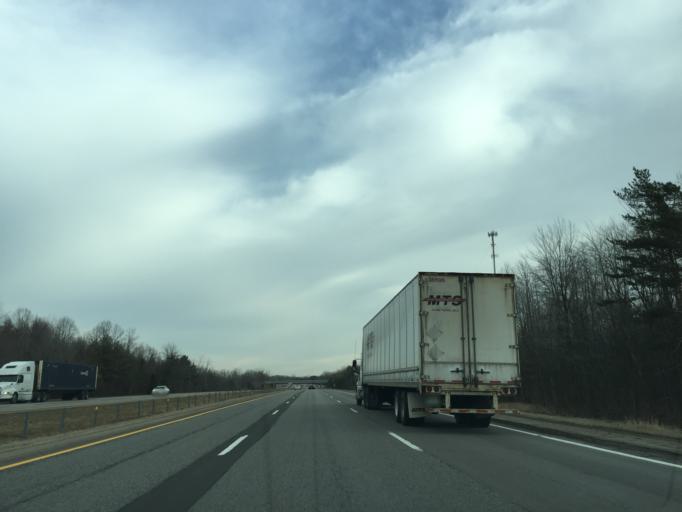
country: US
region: Michigan
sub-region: Berrien County
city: Shorewood-Tower Hills-Harbert
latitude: 41.8609
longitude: -86.6150
